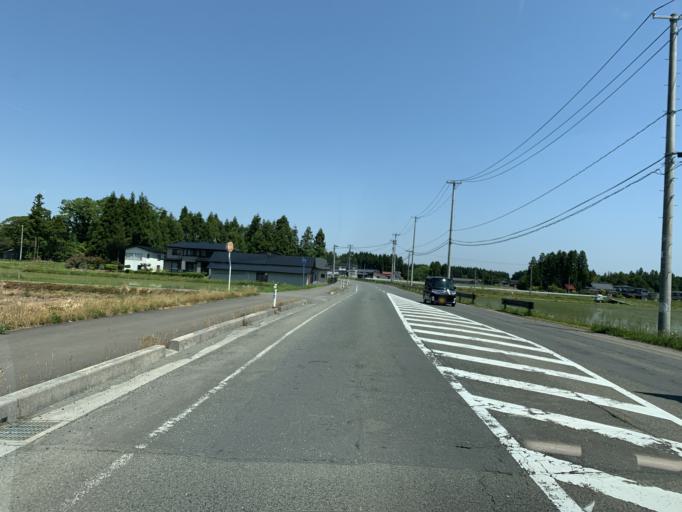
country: JP
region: Iwate
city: Kitakami
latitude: 39.2335
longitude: 141.0669
